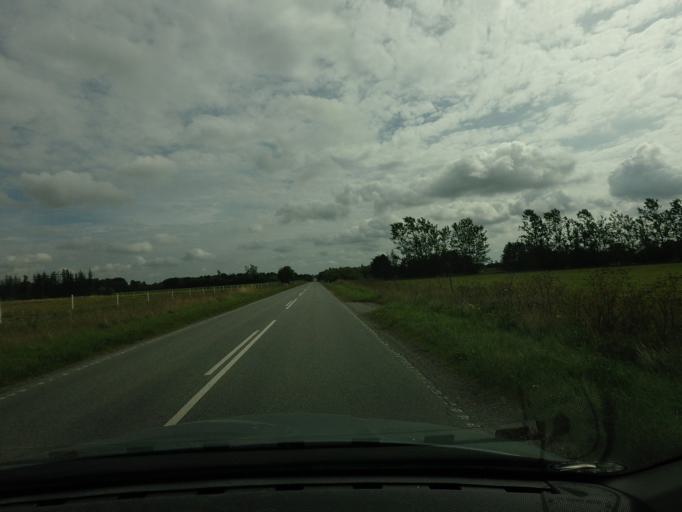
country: DK
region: North Denmark
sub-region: Bronderslev Kommune
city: Dronninglund
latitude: 57.2813
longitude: 10.2816
